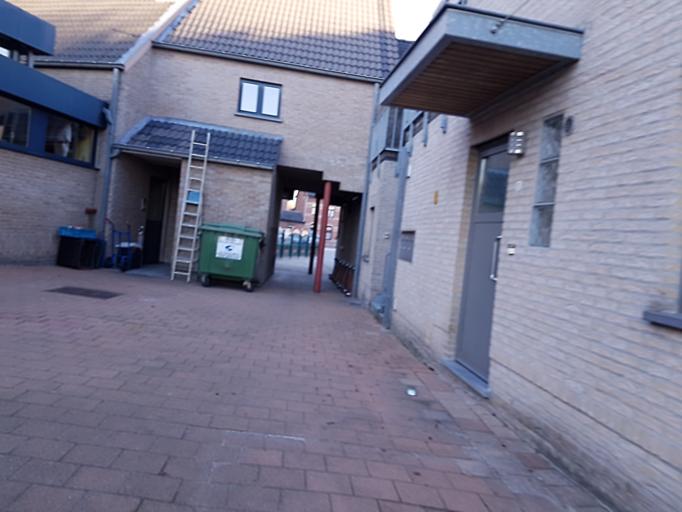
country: BE
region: Flanders
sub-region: Provincie Antwerpen
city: Puurs
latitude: 51.1060
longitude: 4.2986
